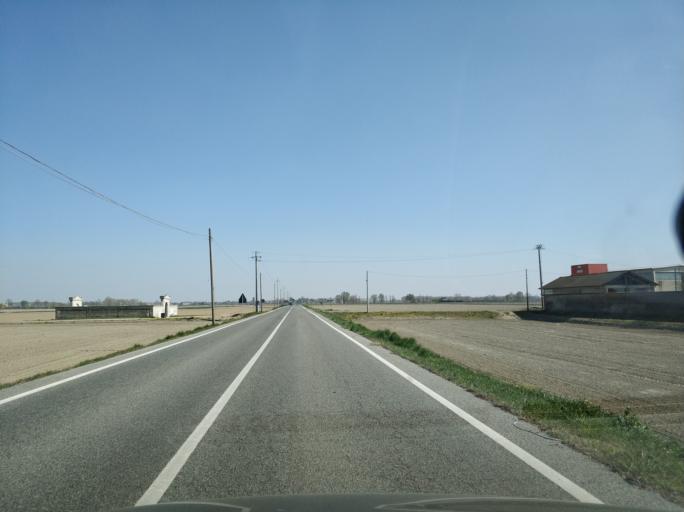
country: IT
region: Piedmont
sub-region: Provincia di Novara
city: Vinzaglio
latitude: 45.3139
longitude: 8.4992
